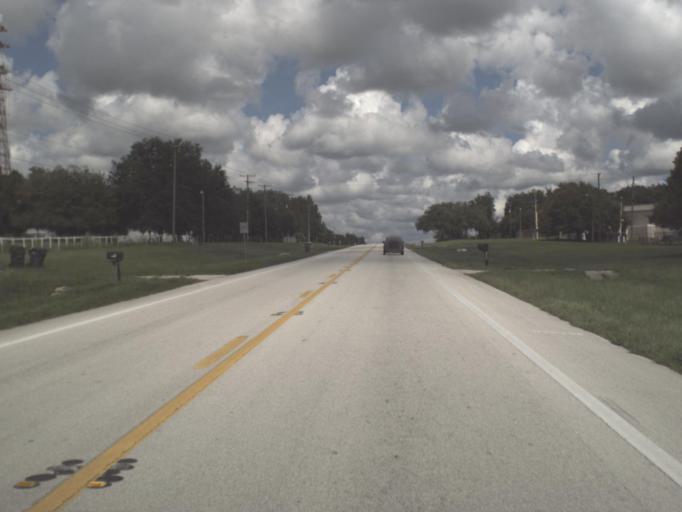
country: US
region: Florida
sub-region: Polk County
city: Polk City
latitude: 28.2923
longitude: -81.8329
